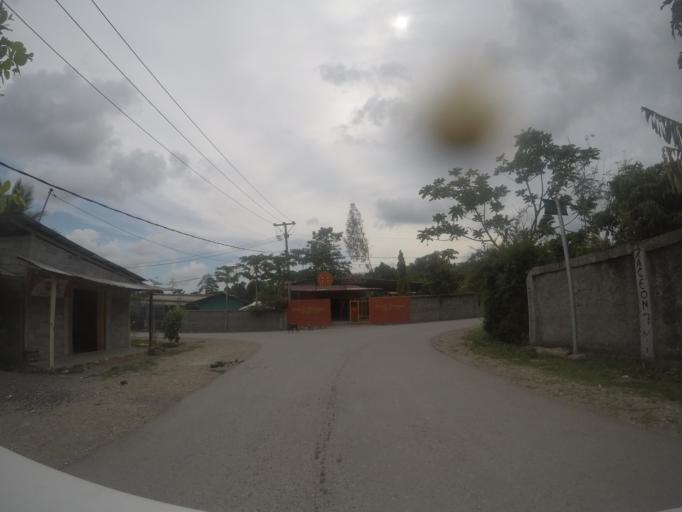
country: TL
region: Viqueque
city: Viqueque
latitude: -8.8704
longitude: 126.3657
